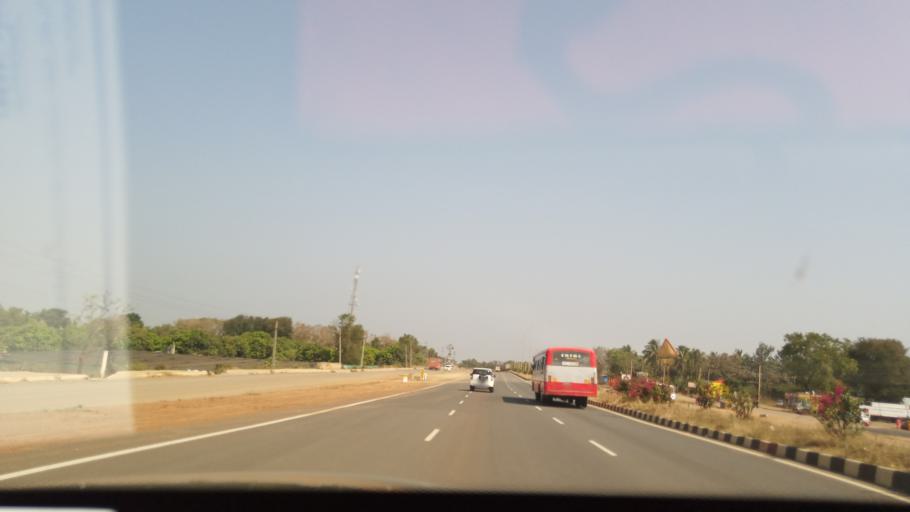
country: IN
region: Karnataka
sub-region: Dharwad
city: Kundgol
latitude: 15.1644
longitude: 75.1412
